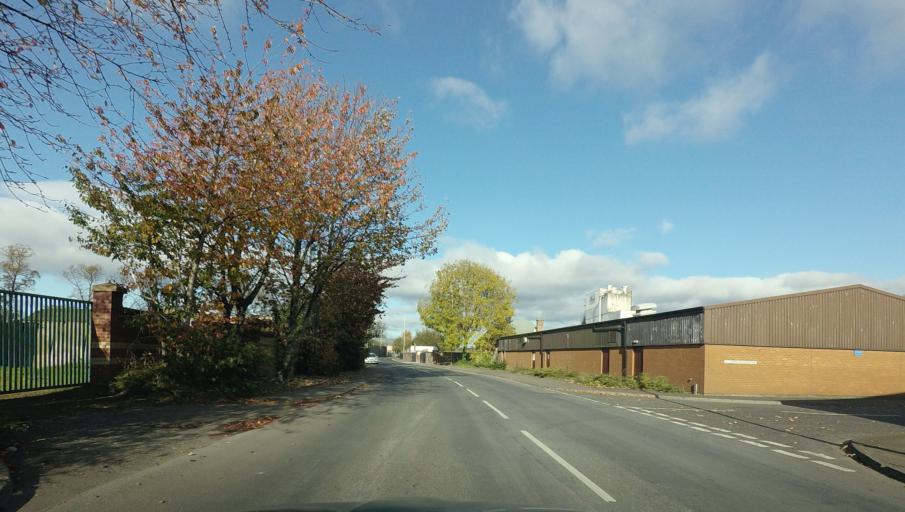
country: GB
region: Scotland
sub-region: Perth and Kinross
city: Perth
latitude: 56.3852
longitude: -3.4268
